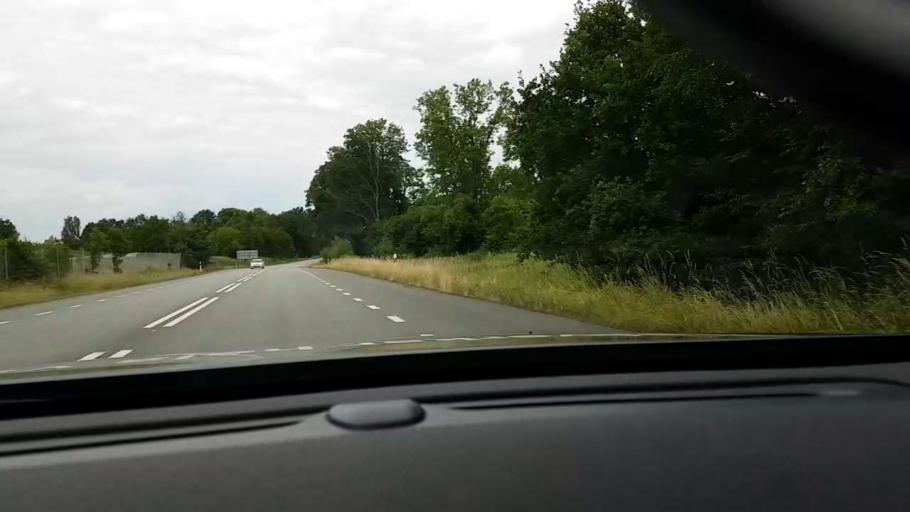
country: SE
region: Skane
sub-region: Hassleholms Kommun
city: Hassleholm
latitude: 56.1431
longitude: 13.8036
